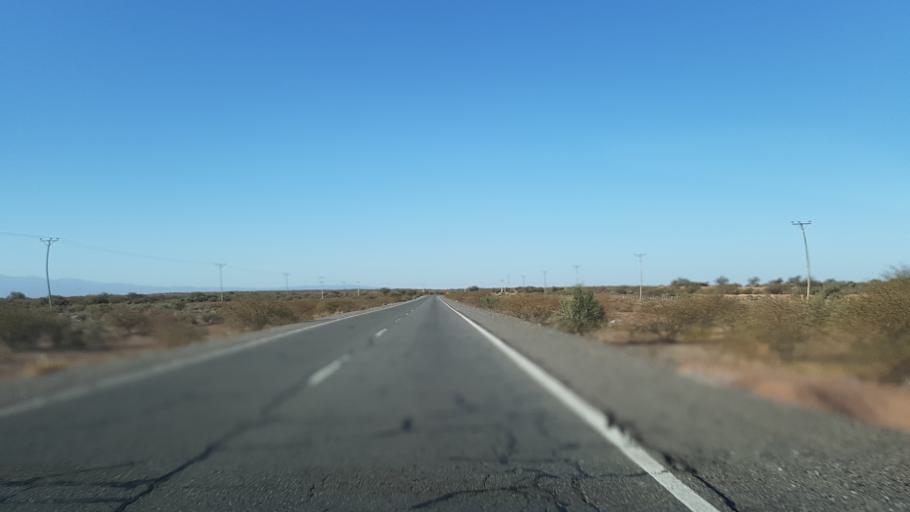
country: AR
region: San Juan
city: Caucete
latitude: -31.6000
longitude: -67.6997
